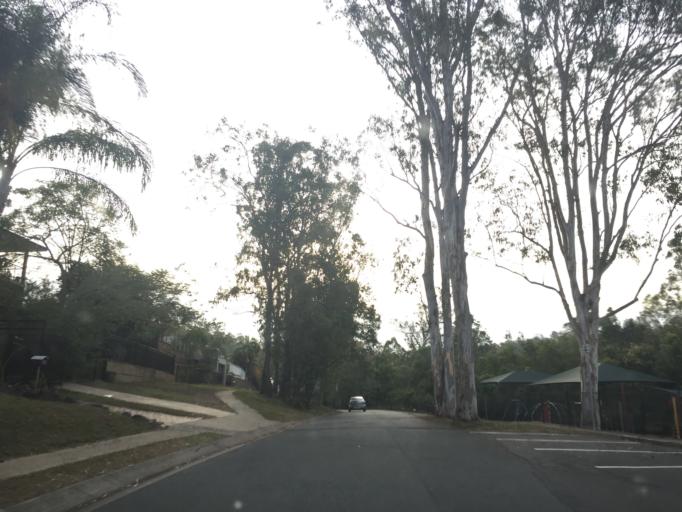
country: AU
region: Queensland
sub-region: Moreton Bay
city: Ferny Hills
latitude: -27.4392
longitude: 152.9350
